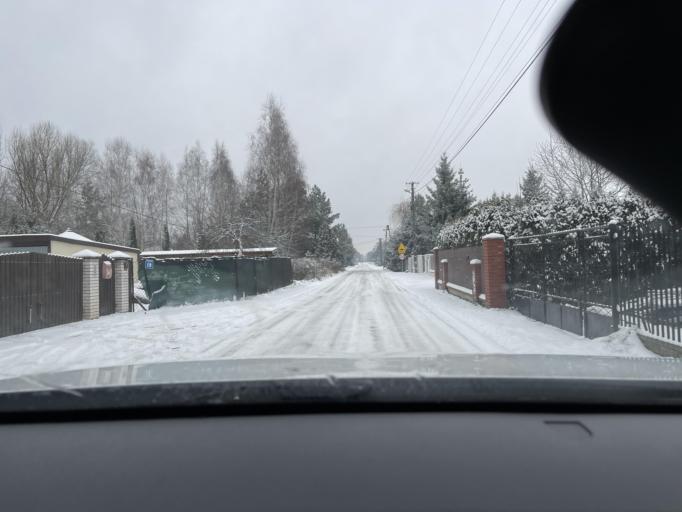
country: PL
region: Masovian Voivodeship
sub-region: Powiat zyrardowski
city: Zyrardow
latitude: 52.0311
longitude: 20.4583
